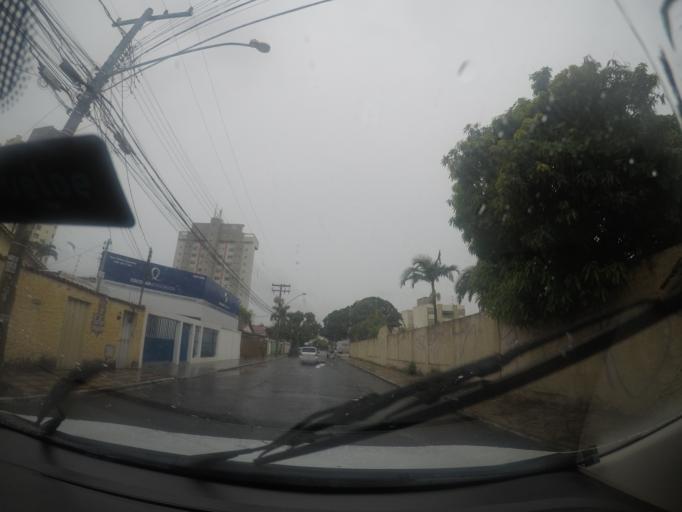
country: BR
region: Goias
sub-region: Goiania
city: Goiania
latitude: -16.6786
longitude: -49.2794
